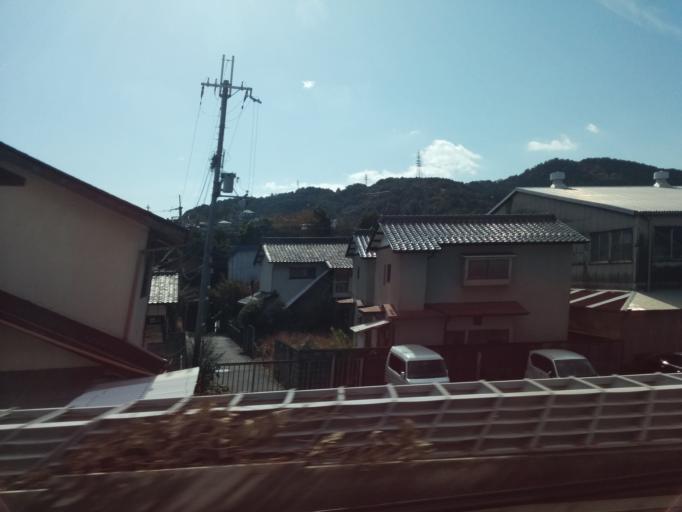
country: JP
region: Shiga Prefecture
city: Otsu-shi
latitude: 34.9722
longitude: 135.8910
